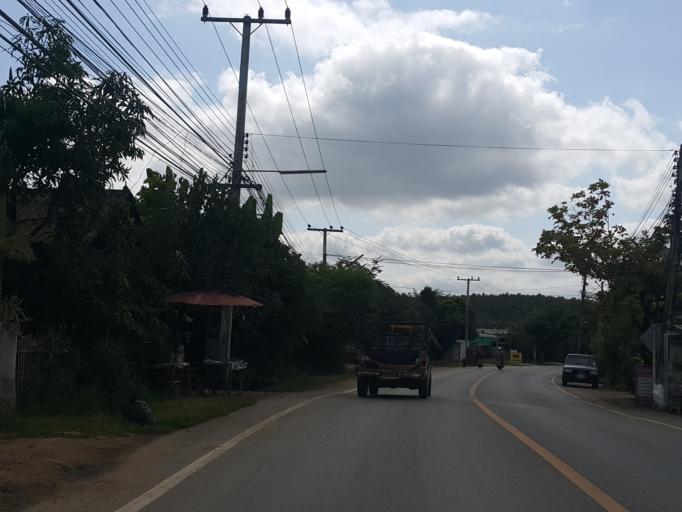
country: TH
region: Lamphun
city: Ban Thi
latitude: 18.6121
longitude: 99.0913
